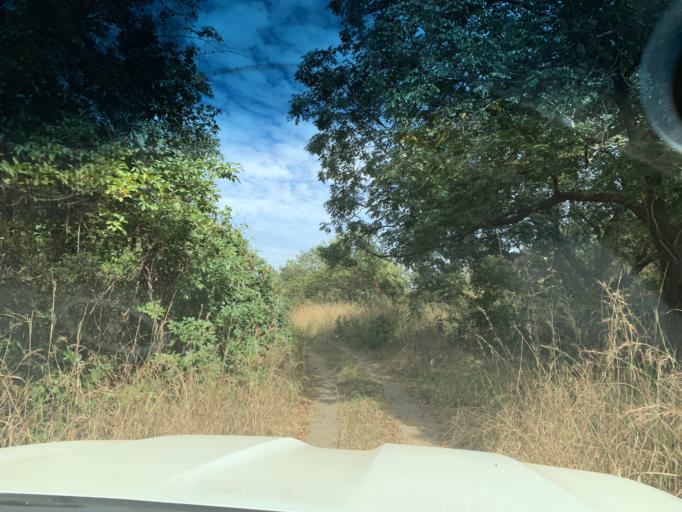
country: GN
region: Mamou
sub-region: Pita
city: Pita
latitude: 10.9921
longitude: -12.4889
